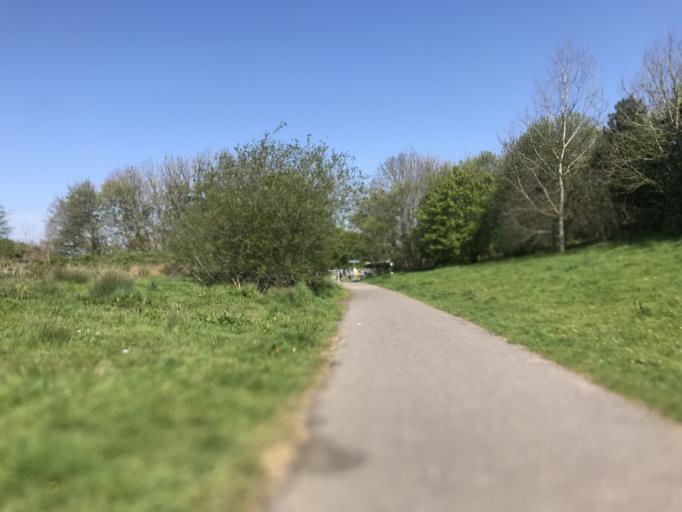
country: GB
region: England
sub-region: Devon
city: Barnstaple
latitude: 51.0712
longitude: -4.0584
